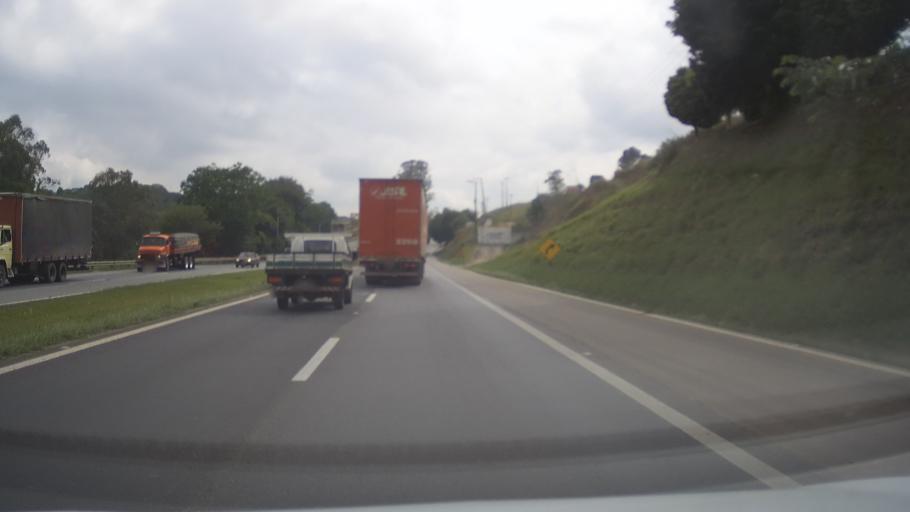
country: BR
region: Minas Gerais
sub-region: Extrema
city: Extrema
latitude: -22.8210
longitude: -46.2999
